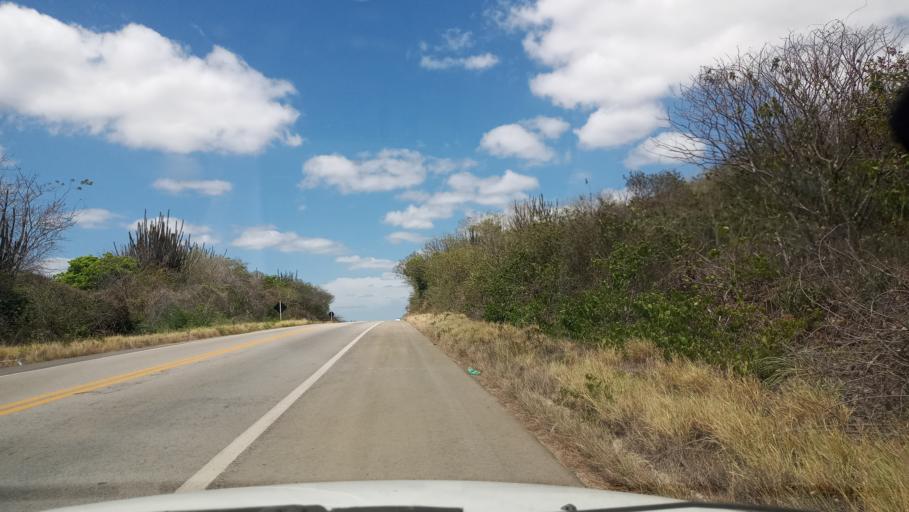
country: BR
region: Rio Grande do Norte
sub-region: Sao Paulo Do Potengi
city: Sao Paulo do Potengi
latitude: -5.7484
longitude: -35.9093
